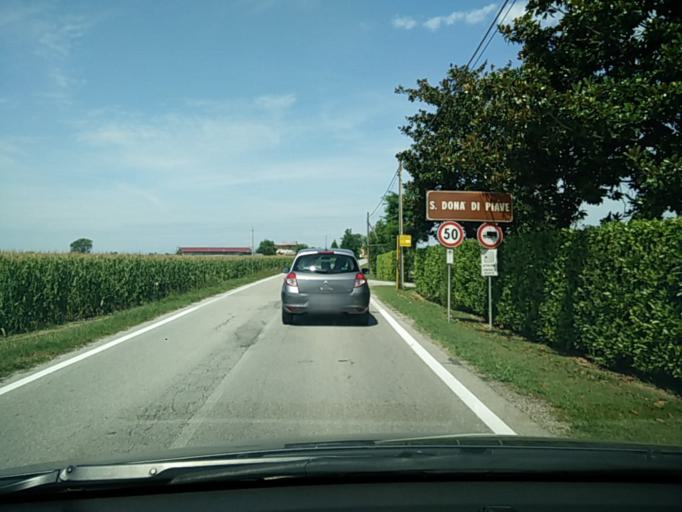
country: IT
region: Veneto
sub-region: Provincia di Venezia
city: Passarella
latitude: 45.5745
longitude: 12.6156
